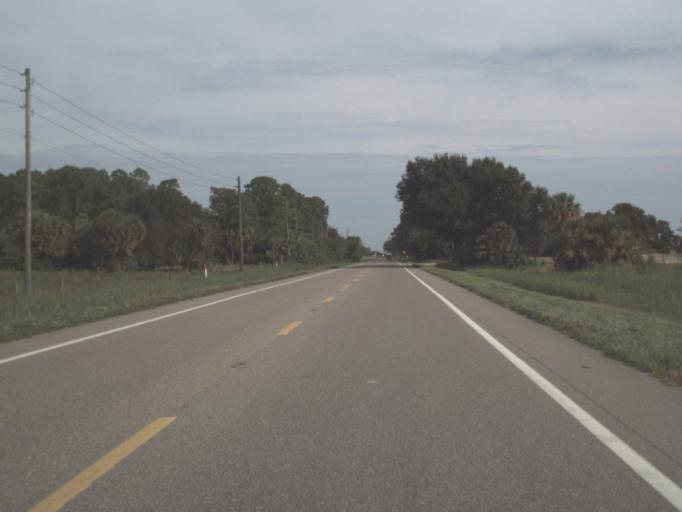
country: US
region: Florida
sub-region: DeSoto County
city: Nocatee
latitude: 27.0104
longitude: -81.7604
